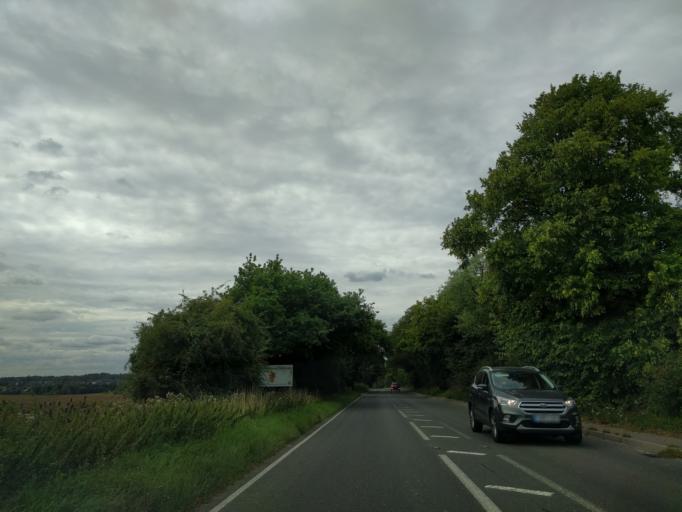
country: GB
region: England
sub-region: Essex
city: Great Dunmow
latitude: 51.8739
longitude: 0.3887
